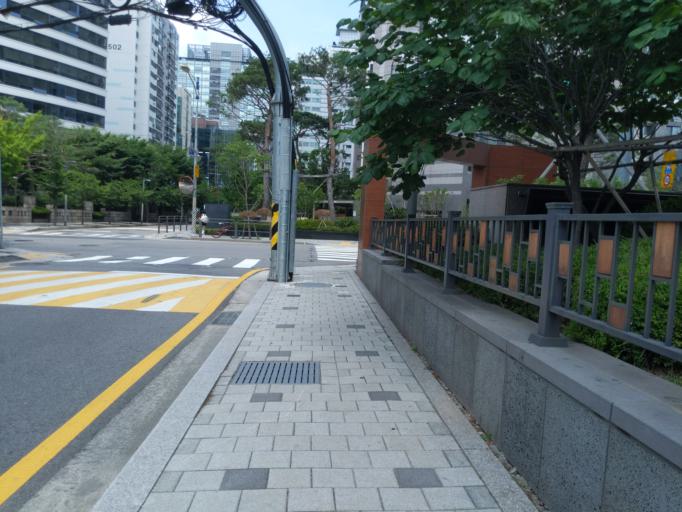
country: KR
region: Seoul
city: Seoul
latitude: 37.4934
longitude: 127.0255
